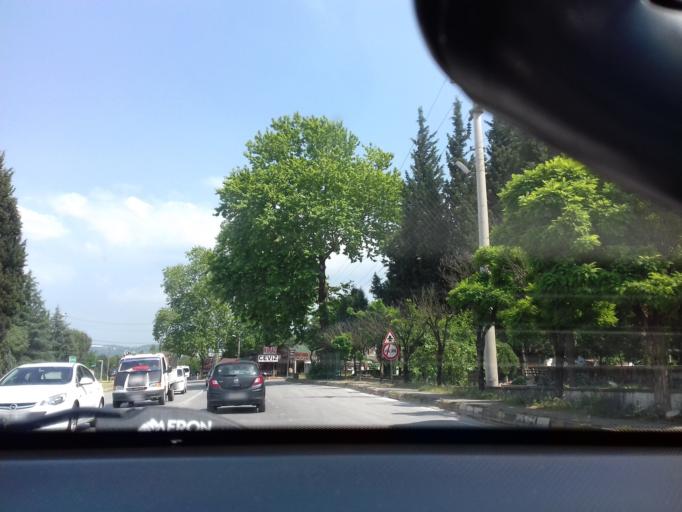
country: TR
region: Sakarya
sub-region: Merkez
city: Sapanca
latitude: 40.6885
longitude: 30.2362
